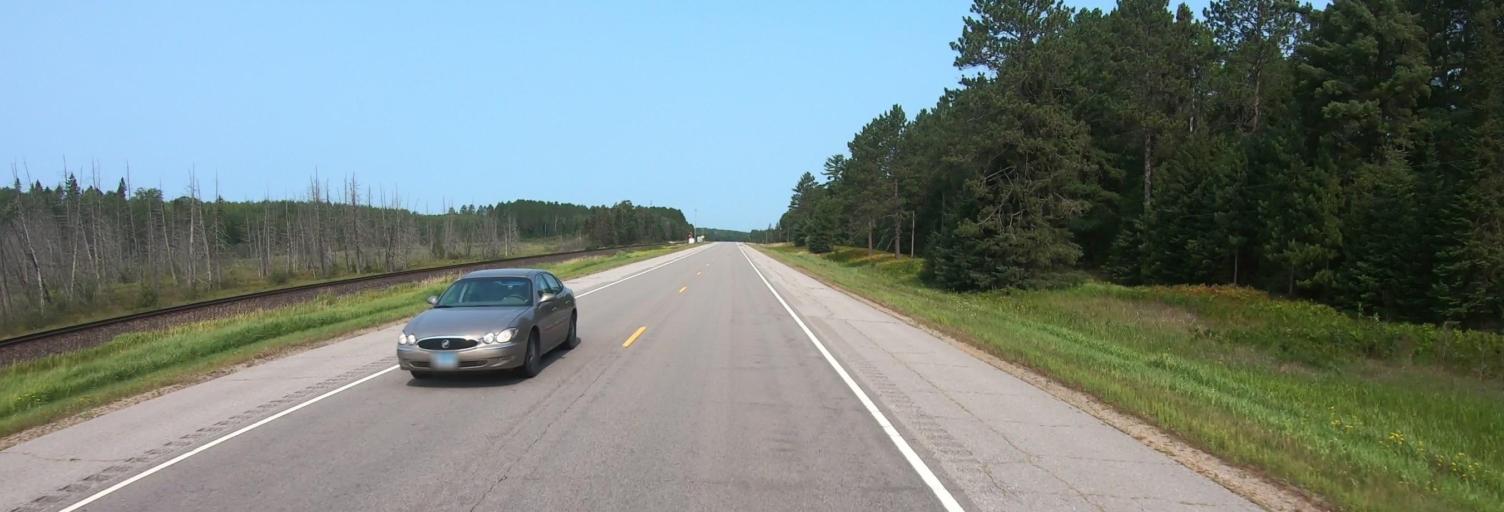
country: US
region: Minnesota
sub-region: Saint Louis County
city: Mountain Iron
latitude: 48.1376
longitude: -92.8539
